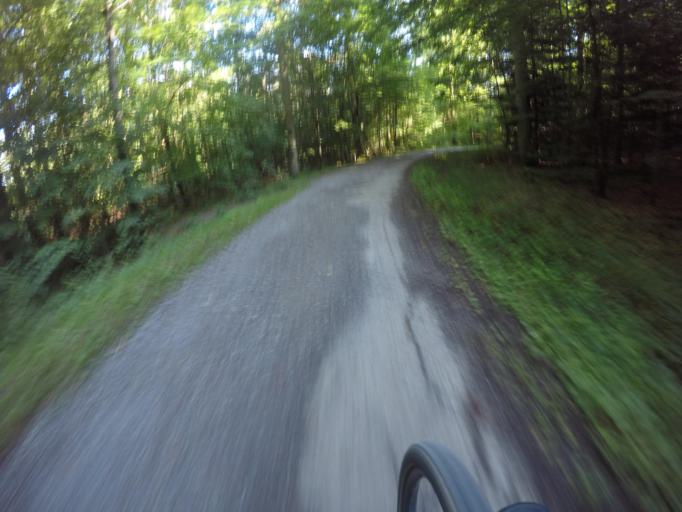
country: DE
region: Baden-Wuerttemberg
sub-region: Regierungsbezirk Stuttgart
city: Stuttgart
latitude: 48.7567
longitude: 9.1232
